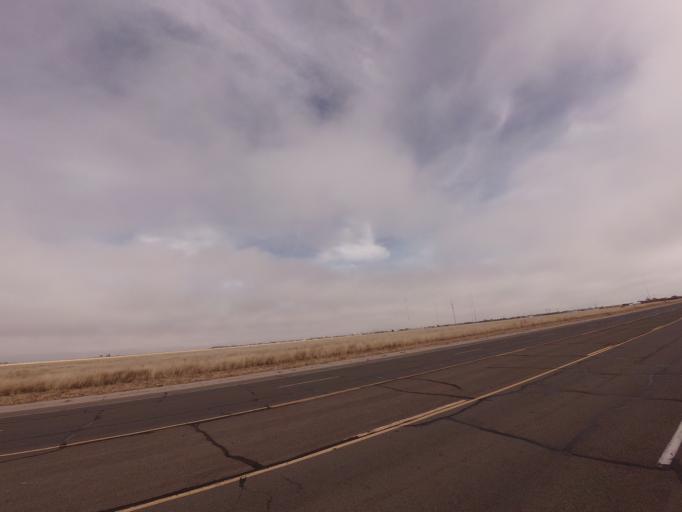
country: US
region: New Mexico
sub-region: Curry County
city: Clovis
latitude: 34.4340
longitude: -103.2205
